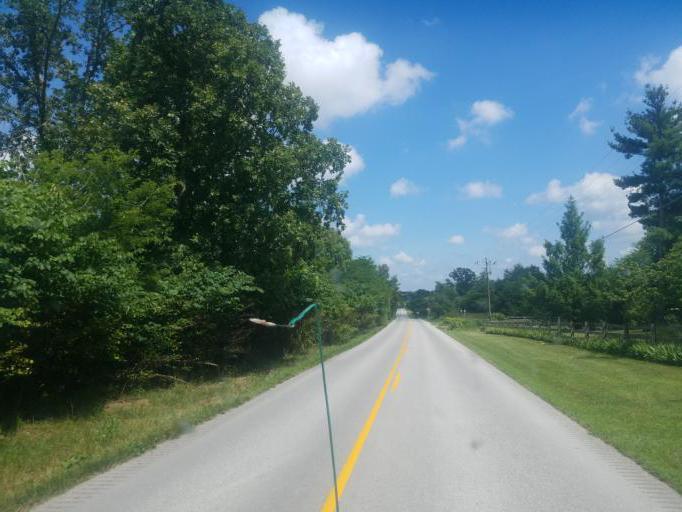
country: US
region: Kentucky
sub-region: Hart County
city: Munfordville
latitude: 37.3077
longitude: -86.0664
